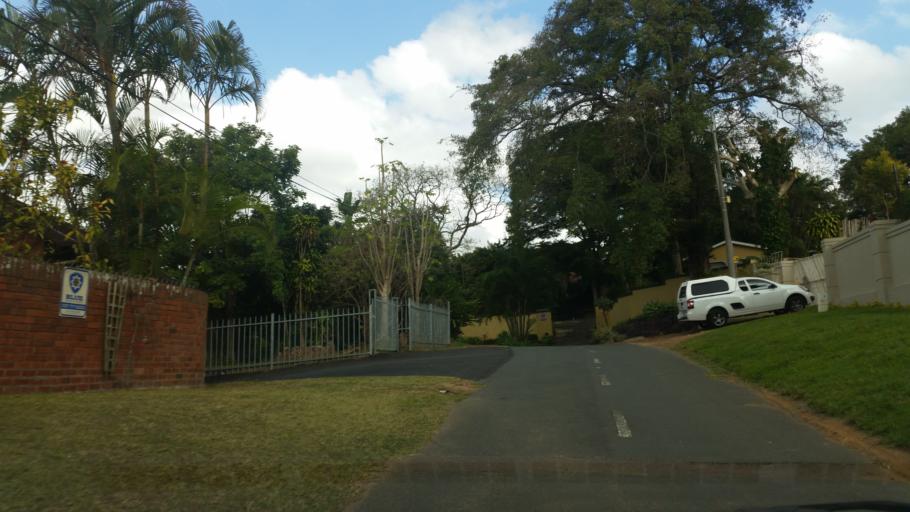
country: ZA
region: KwaZulu-Natal
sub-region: eThekwini Metropolitan Municipality
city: Berea
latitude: -29.8311
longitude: 30.9237
